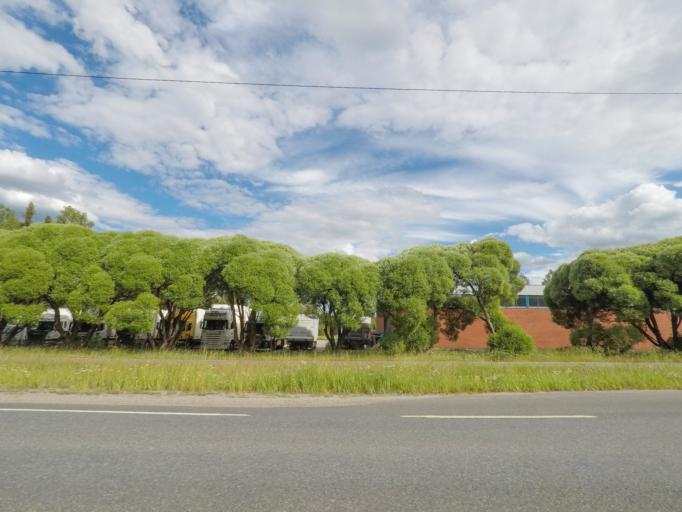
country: FI
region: Paijanne Tavastia
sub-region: Lahti
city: Lahti
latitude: 60.9484
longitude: 25.6085
